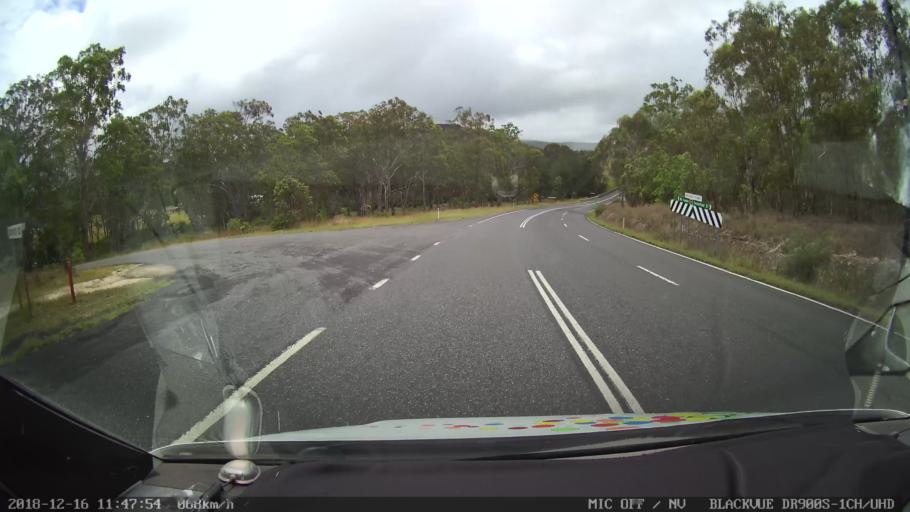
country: AU
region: New South Wales
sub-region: Tenterfield Municipality
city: Carrolls Creek
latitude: -28.9203
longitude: 152.2429
